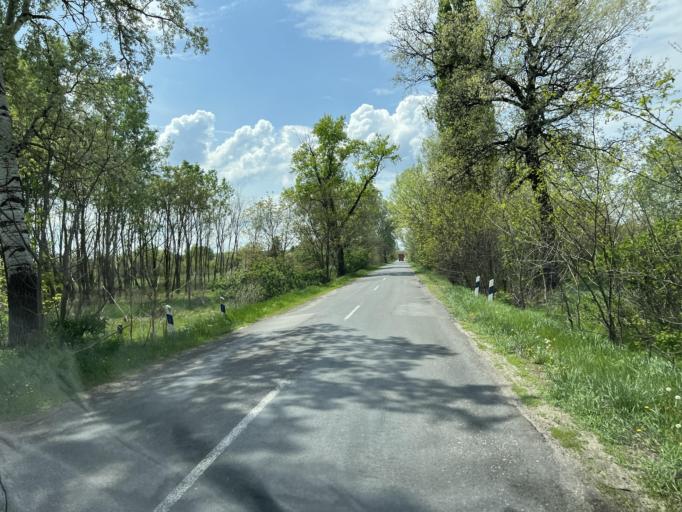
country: HU
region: Pest
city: Csemo
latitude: 47.1332
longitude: 19.7199
